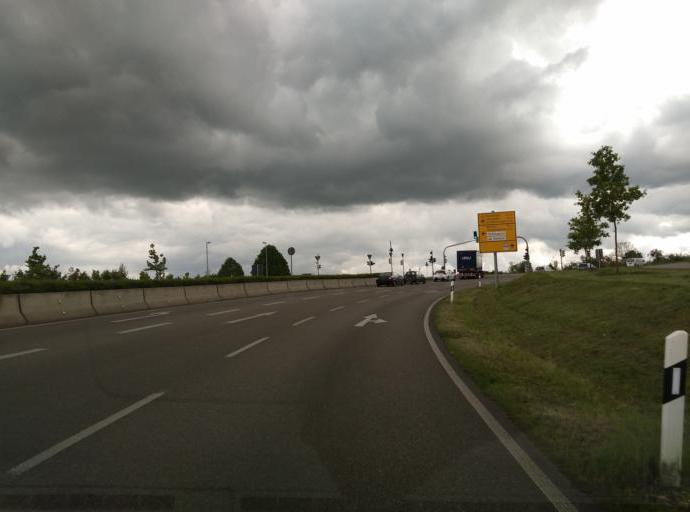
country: DE
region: Baden-Wuerttemberg
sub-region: Regierungsbezirk Stuttgart
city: Nurtingen
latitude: 48.6184
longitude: 9.3275
